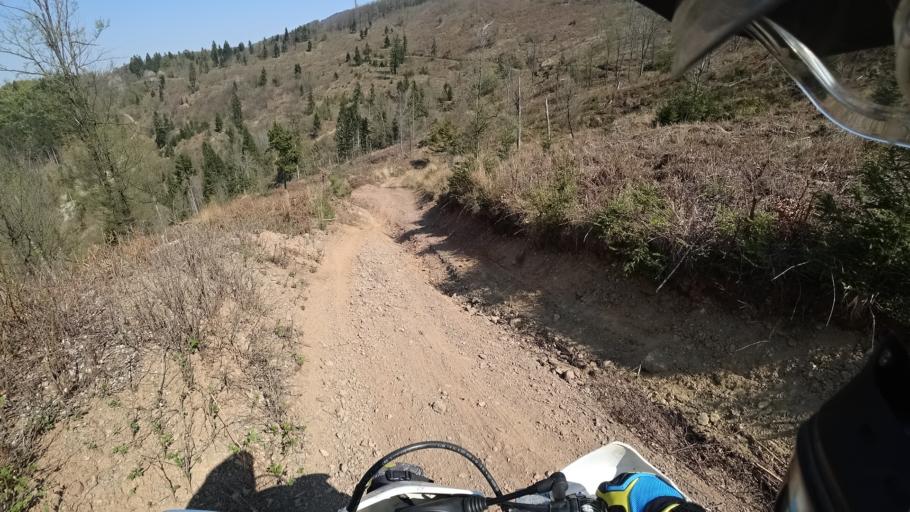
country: HR
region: Zagrebacka
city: Jablanovec
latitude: 45.8893
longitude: 15.9153
